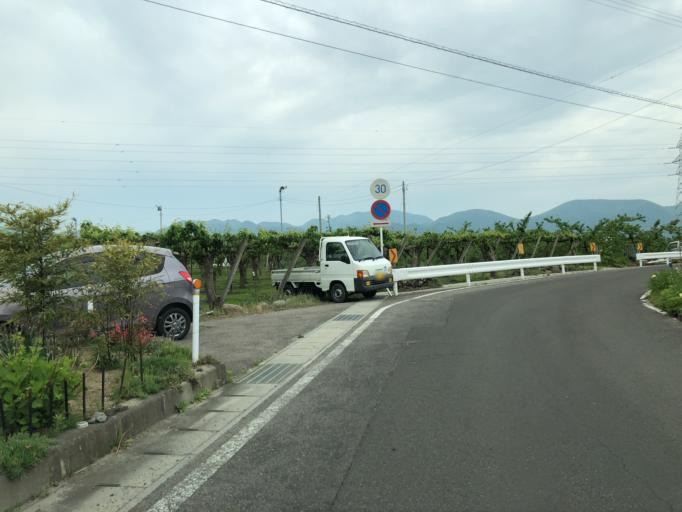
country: JP
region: Fukushima
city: Fukushima-shi
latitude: 37.7841
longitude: 140.4214
